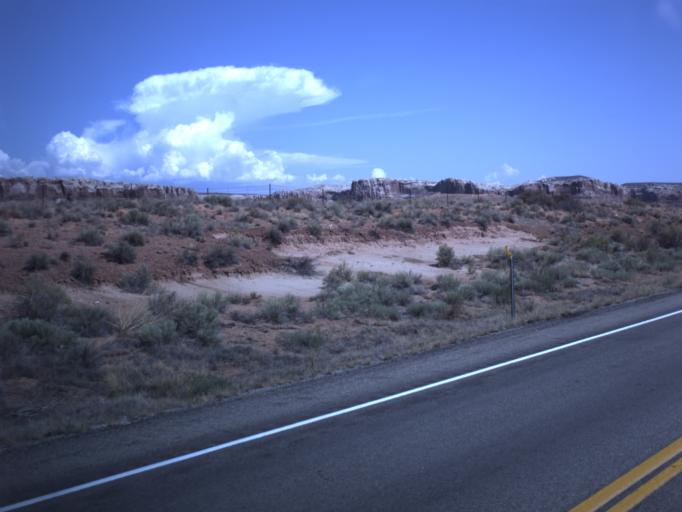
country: US
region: Utah
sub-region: San Juan County
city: Blanding
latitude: 37.2701
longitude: -109.5987
